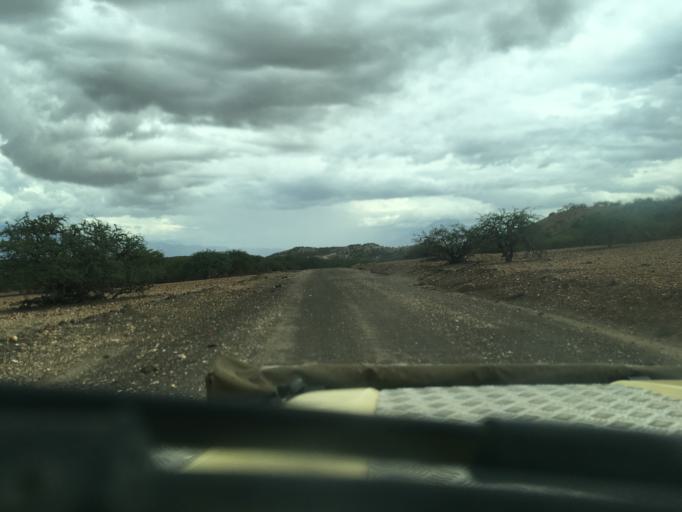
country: KE
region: Kajiado
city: Magadi
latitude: -2.4012
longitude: 35.8724
